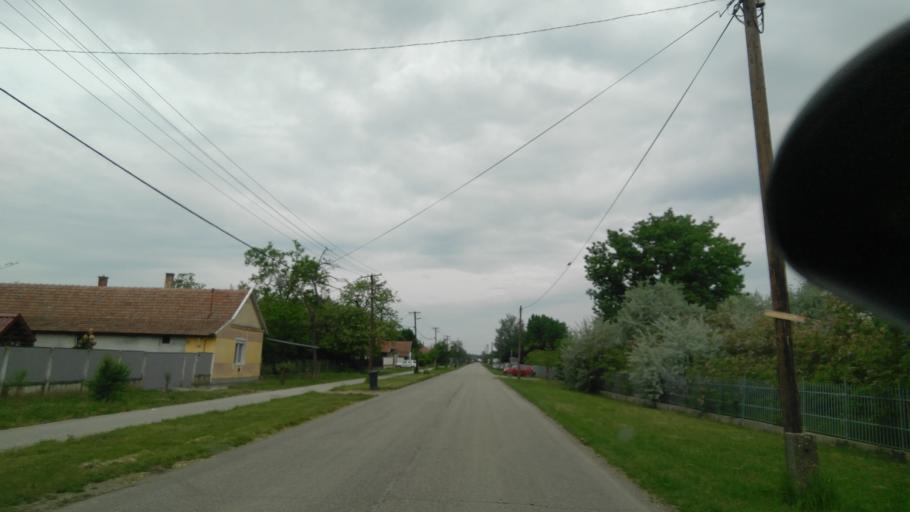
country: HU
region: Bekes
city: Veszto
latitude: 46.9148
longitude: 21.2571
